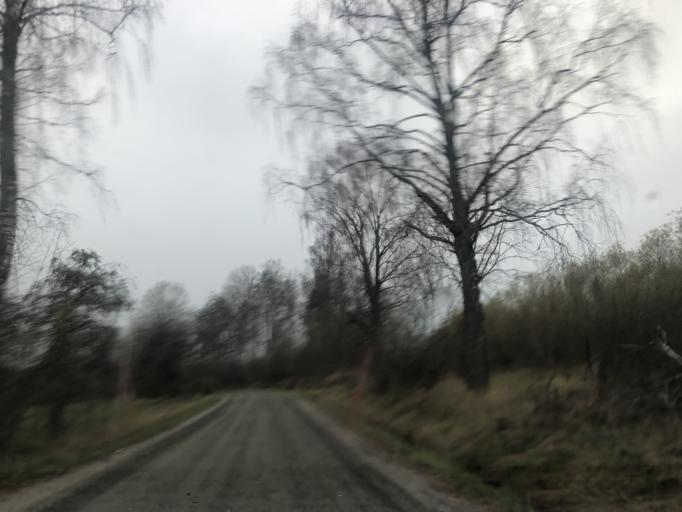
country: SE
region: Vaestra Goetaland
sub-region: Tranemo Kommun
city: Limmared
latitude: 57.6554
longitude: 13.3571
